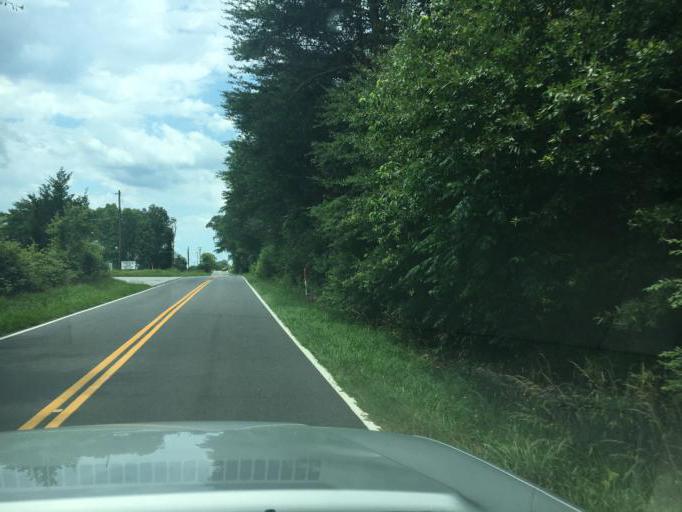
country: US
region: South Carolina
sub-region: Spartanburg County
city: Duncan
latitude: 34.8762
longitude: -82.1796
